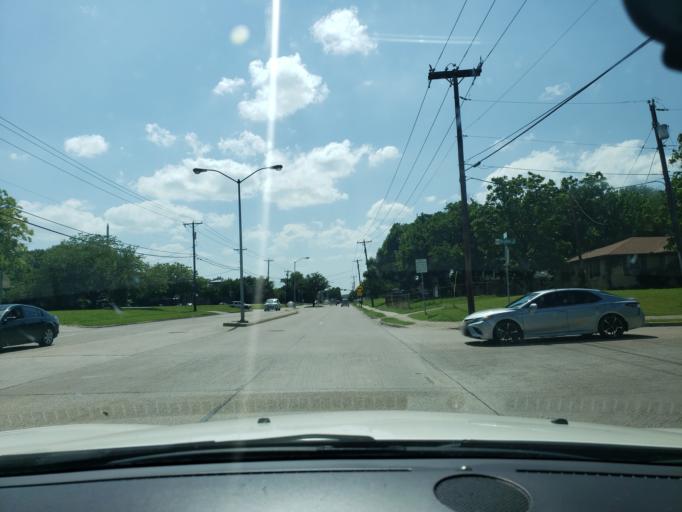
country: US
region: Texas
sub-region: Dallas County
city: Rowlett
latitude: 32.8939
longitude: -96.5629
